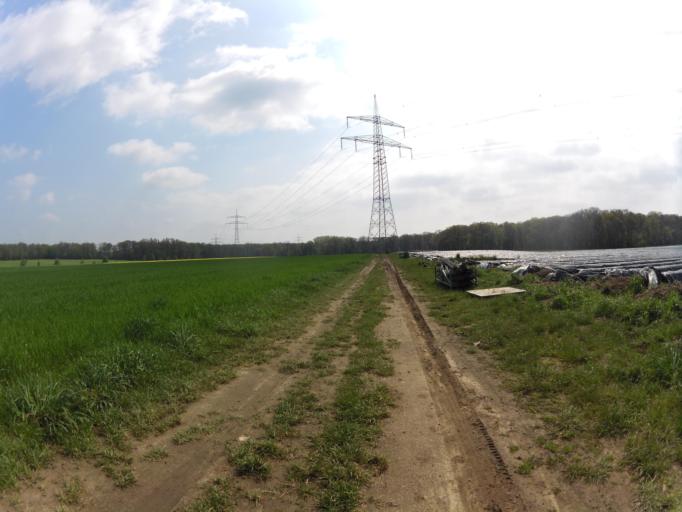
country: DE
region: Bavaria
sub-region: Regierungsbezirk Unterfranken
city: Sommerhausen
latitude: 49.7085
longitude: 10.0657
